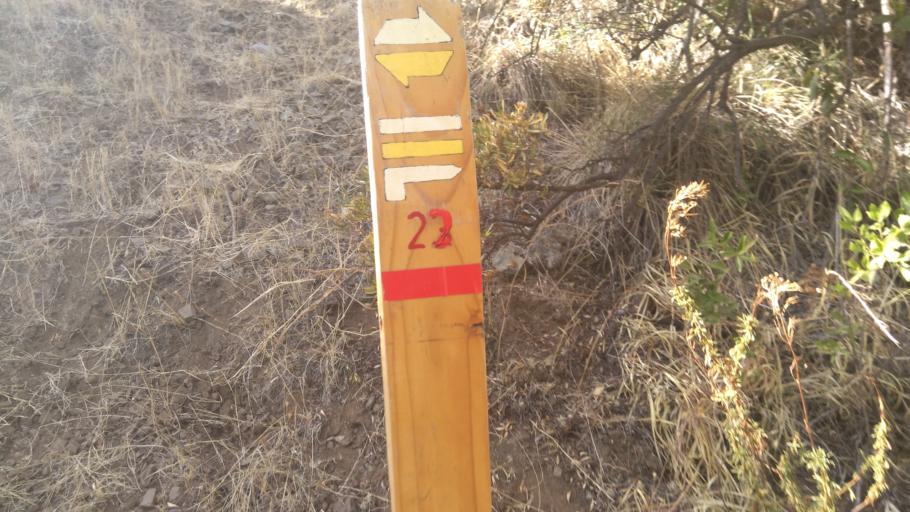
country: CL
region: Santiago Metropolitan
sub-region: Provincia de Cordillera
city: Puente Alto
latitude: -33.7107
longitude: -70.4539
